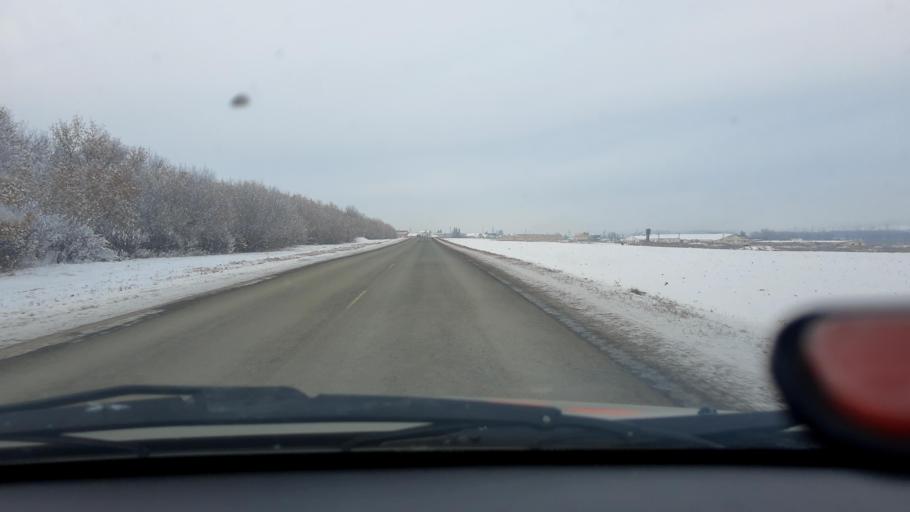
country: RU
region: Bashkortostan
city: Avdon
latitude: 54.4048
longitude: 55.8056
